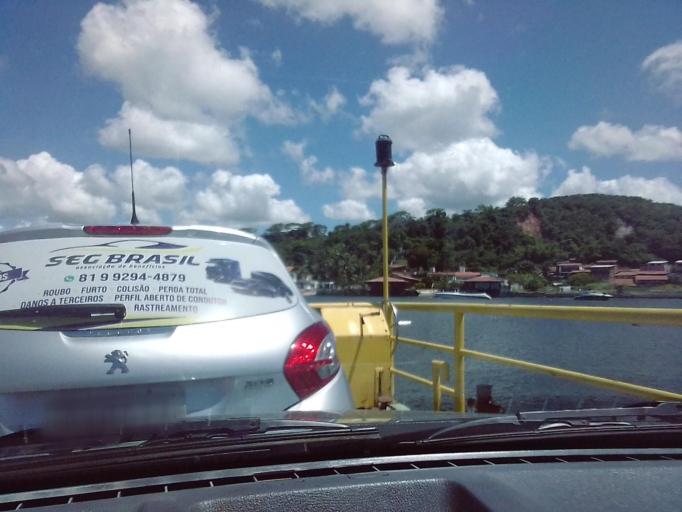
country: BR
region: Pernambuco
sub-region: Igarassu
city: Igarassu
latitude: -7.8531
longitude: -34.8412
